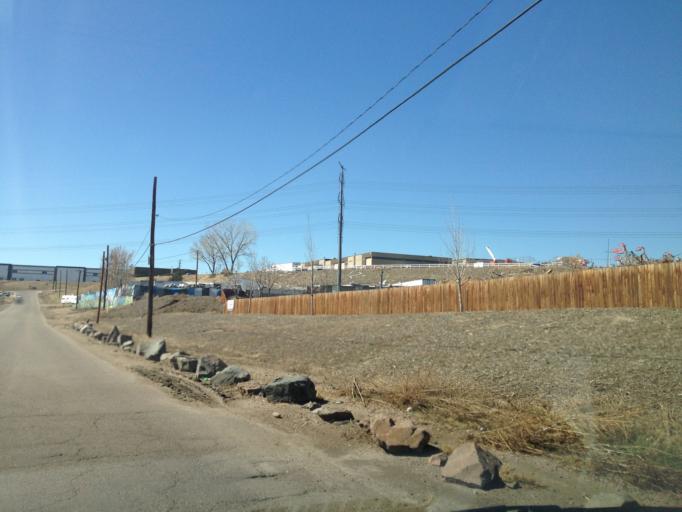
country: US
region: Colorado
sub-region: Adams County
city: Twin Lakes
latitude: 39.7956
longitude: -104.9743
